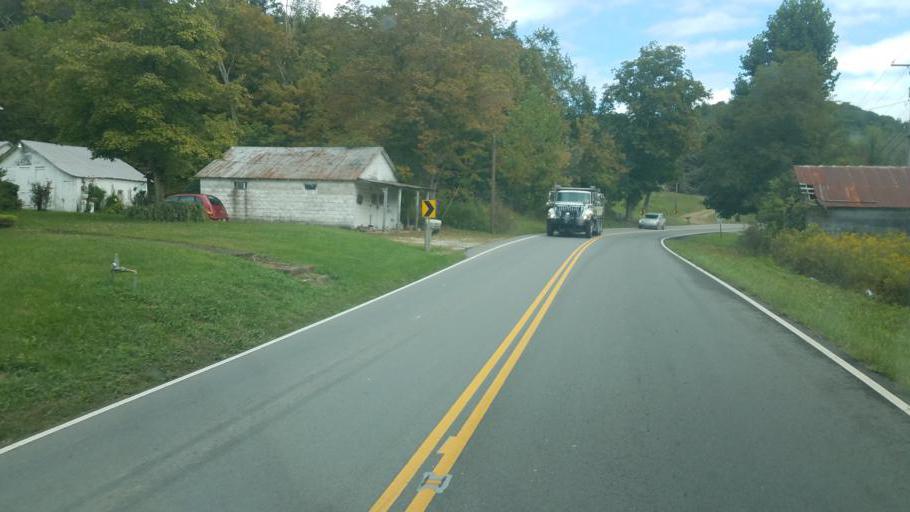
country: US
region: Ohio
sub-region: Scioto County
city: Lucasville
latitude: 38.8716
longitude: -82.9489
